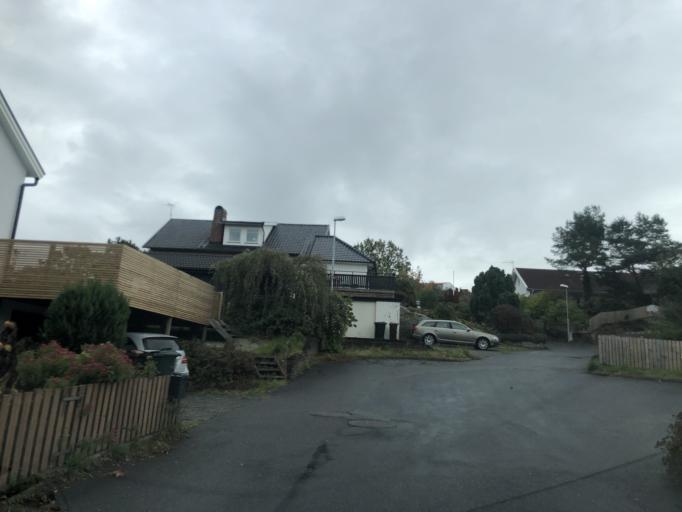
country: SE
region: Vaestra Goetaland
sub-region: Goteborg
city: Majorna
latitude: 57.6743
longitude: 11.8892
